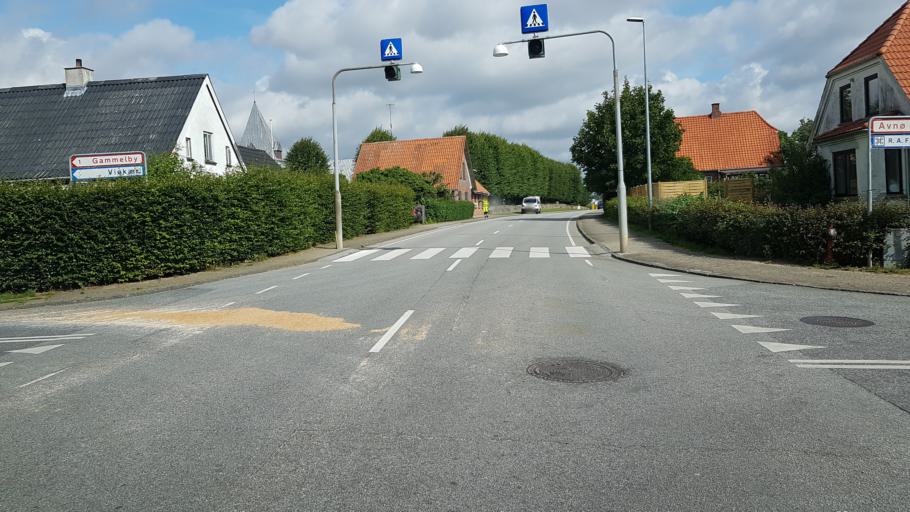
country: DK
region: South Denmark
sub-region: Haderslev Kommune
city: Starup
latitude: 55.3196
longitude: 9.5615
